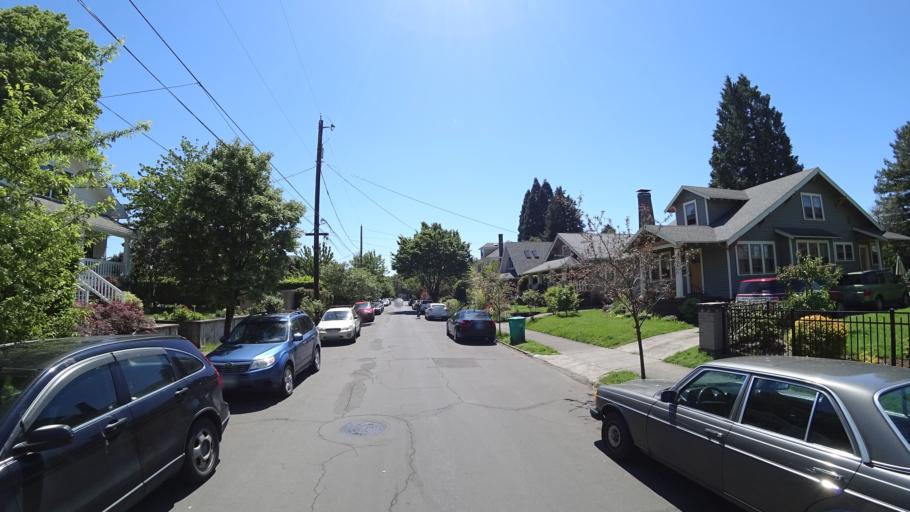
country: US
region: Oregon
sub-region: Multnomah County
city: Portland
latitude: 45.5061
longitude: -122.6327
